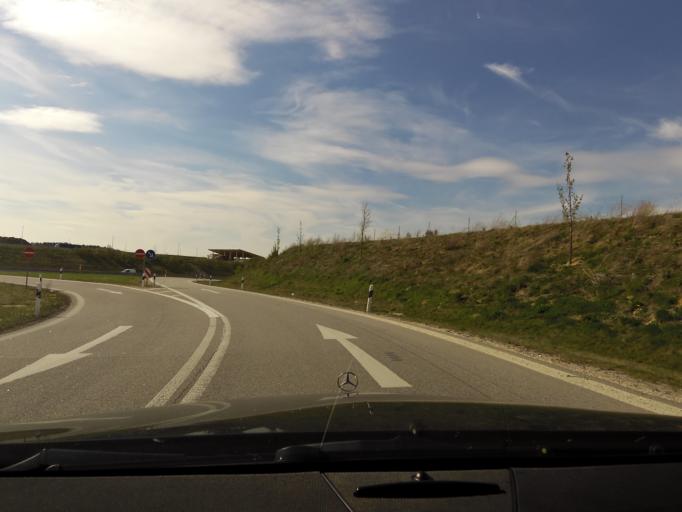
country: DE
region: Bavaria
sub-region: Upper Palatinate
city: Schierling
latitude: 48.8203
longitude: 12.1351
